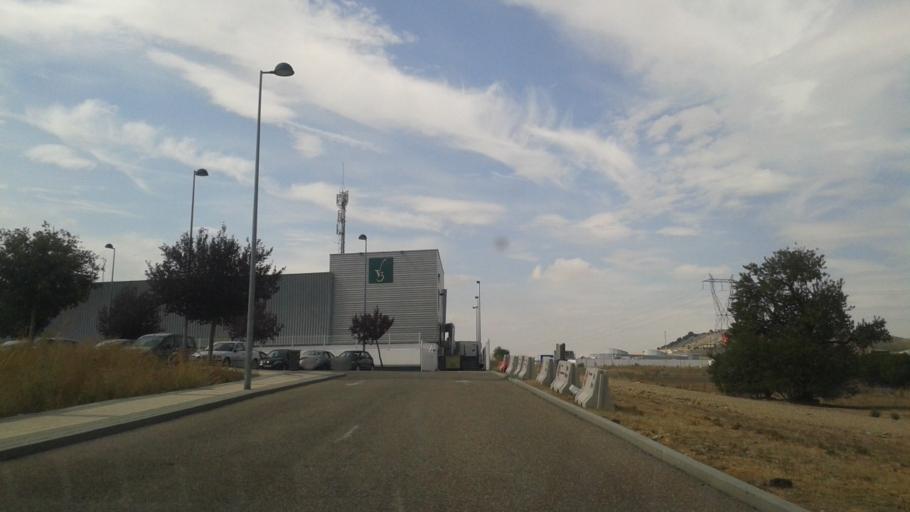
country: ES
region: Castille and Leon
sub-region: Provincia de Valladolid
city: Arroyo
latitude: 41.6302
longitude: -4.7767
